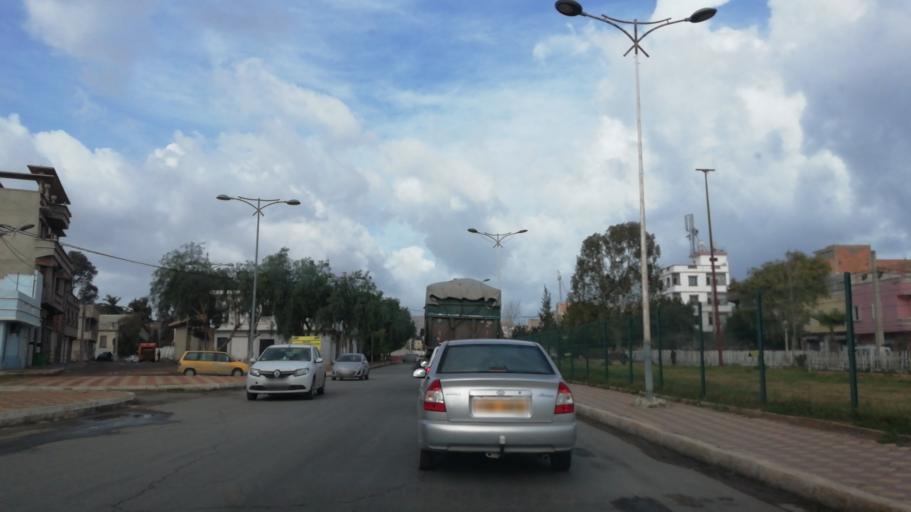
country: DZ
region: Oran
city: Oran
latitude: 35.6770
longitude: -0.6193
